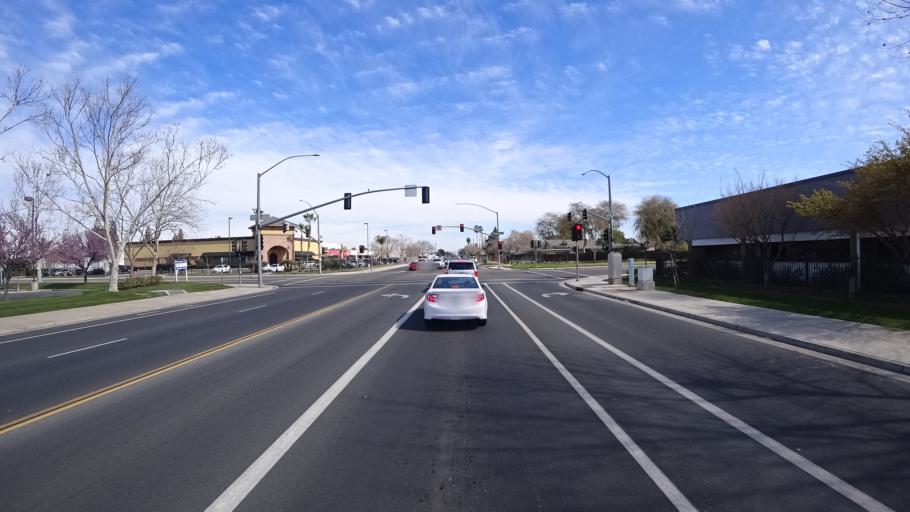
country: US
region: California
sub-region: Fresno County
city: Fresno
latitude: 36.8444
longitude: -119.8023
